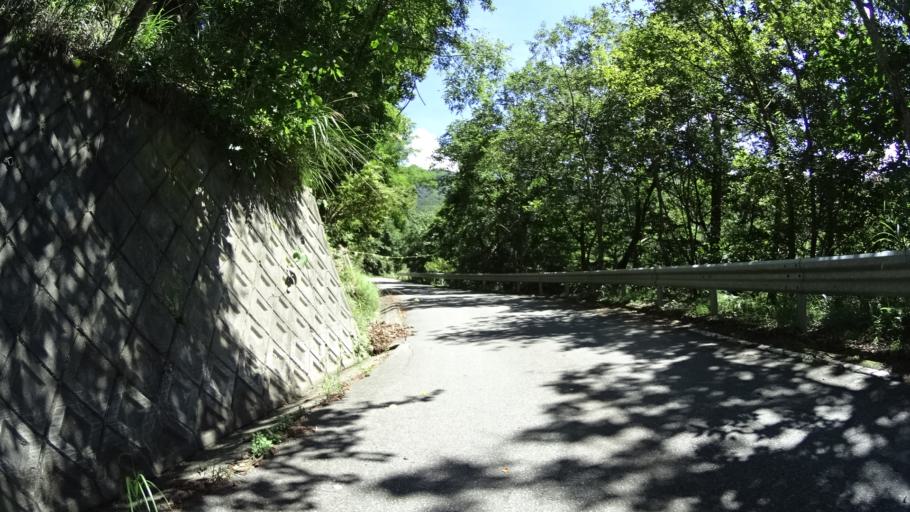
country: JP
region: Yamanashi
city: Enzan
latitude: 35.7428
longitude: 138.8224
